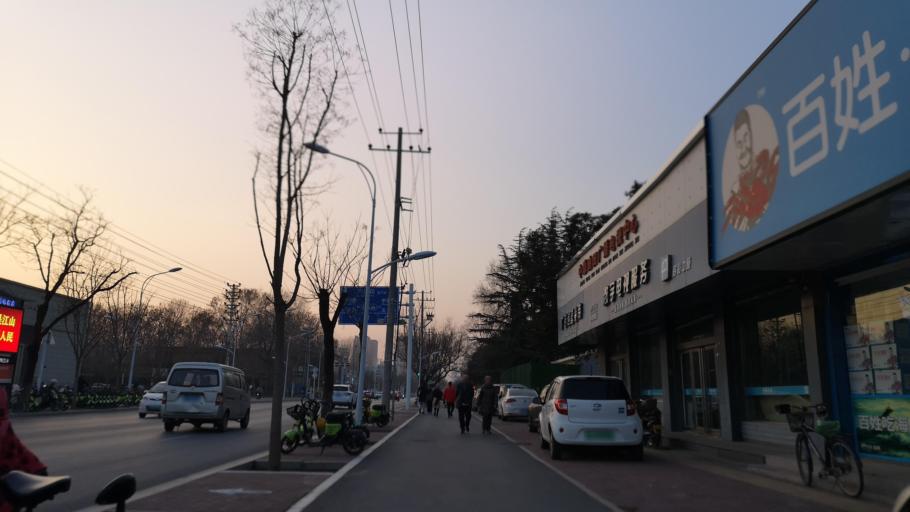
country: CN
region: Henan Sheng
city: Zhongyuanlu
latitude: 35.7721
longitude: 115.0770
